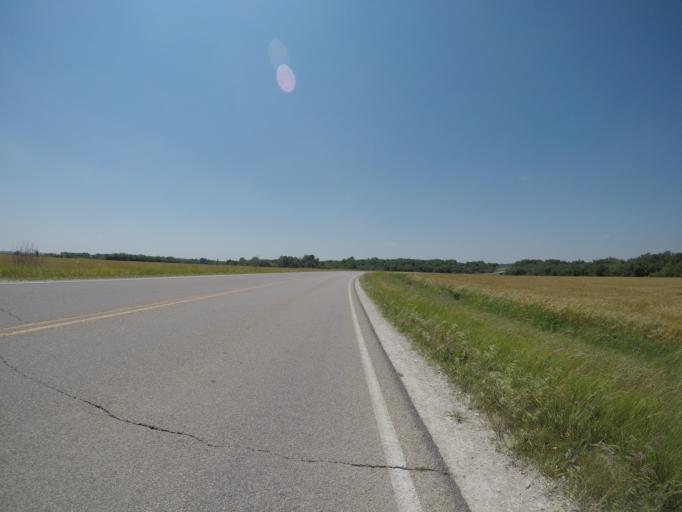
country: US
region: Kansas
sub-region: Pottawatomie County
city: Westmoreland
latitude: 39.2896
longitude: -96.4406
